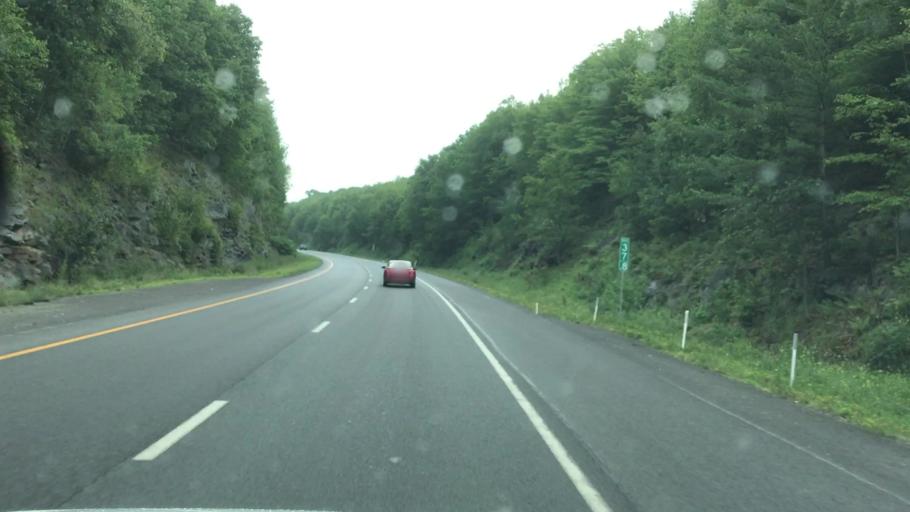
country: US
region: Pennsylvania
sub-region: Pike County
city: Conashaugh Lakes
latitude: 41.3459
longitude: -74.9928
